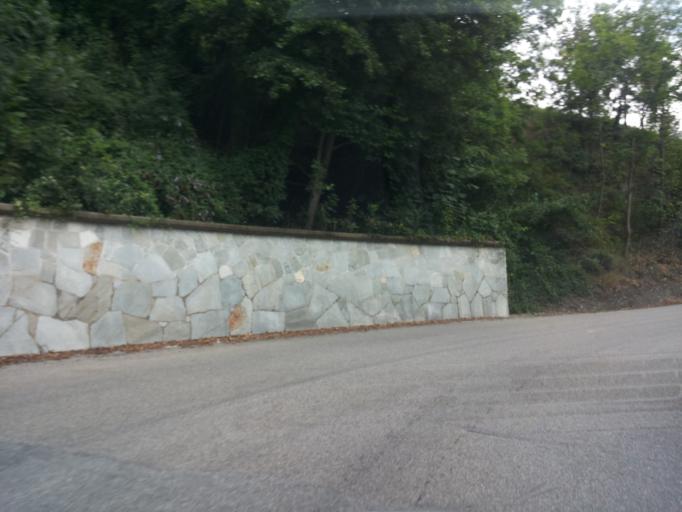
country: IT
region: Piedmont
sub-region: Provincia di Biella
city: Pollone
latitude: 45.5978
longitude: 7.9989
